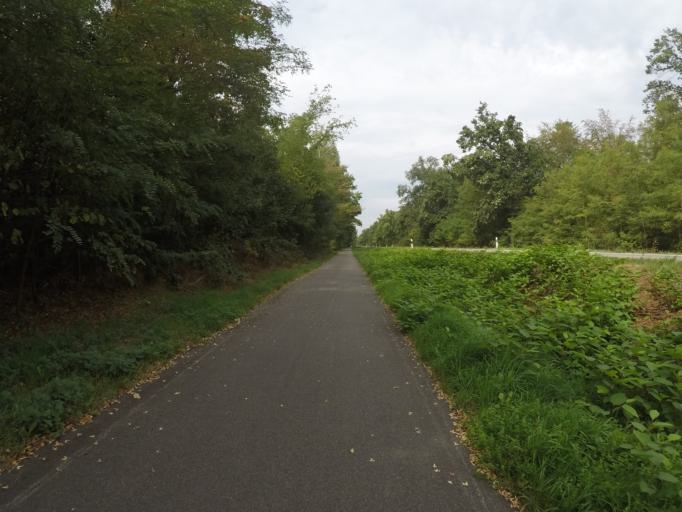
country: DE
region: Rheinland-Pfalz
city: Hanhofen
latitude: 49.3551
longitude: 8.3356
